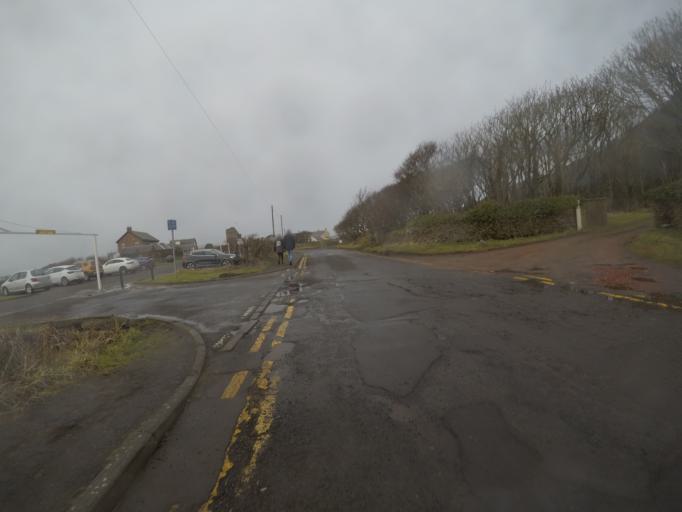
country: GB
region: Scotland
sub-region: North Ayrshire
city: West Kilbride
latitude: 55.6983
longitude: -4.9023
